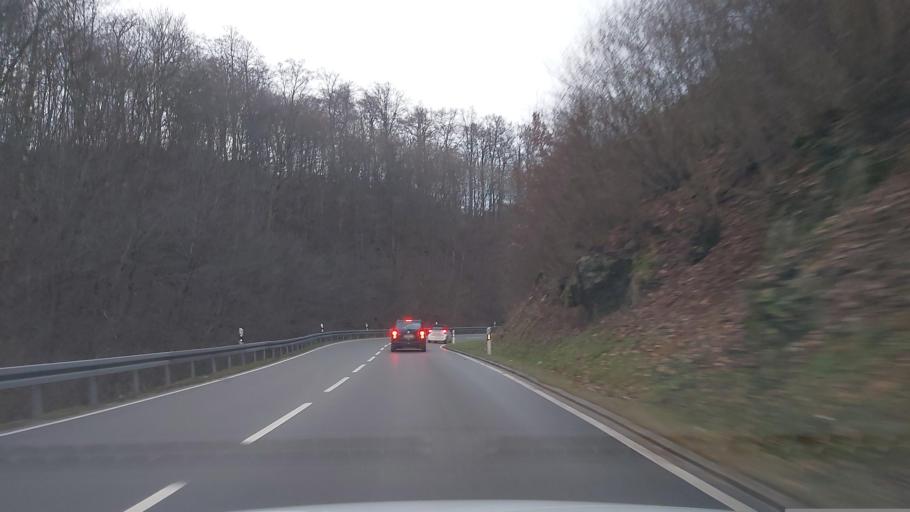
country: DE
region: Baden-Wuerttemberg
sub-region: Tuebingen Region
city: Munsingen
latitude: 48.4351
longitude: 9.4614
